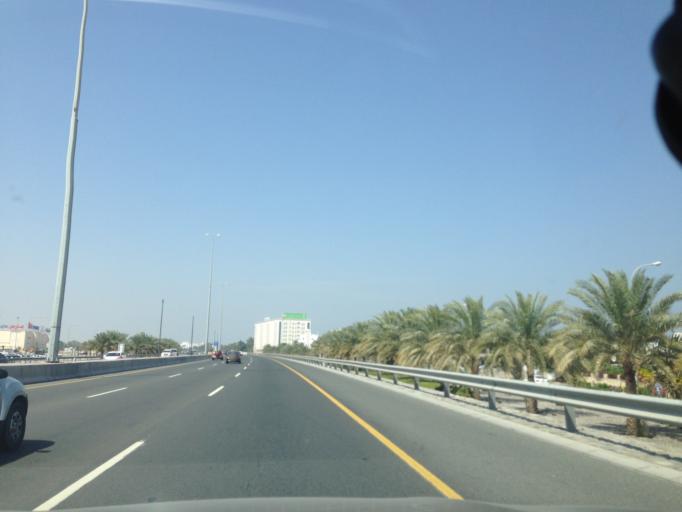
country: OM
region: Muhafazat Masqat
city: As Sib al Jadidah
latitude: 23.6474
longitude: 58.2187
